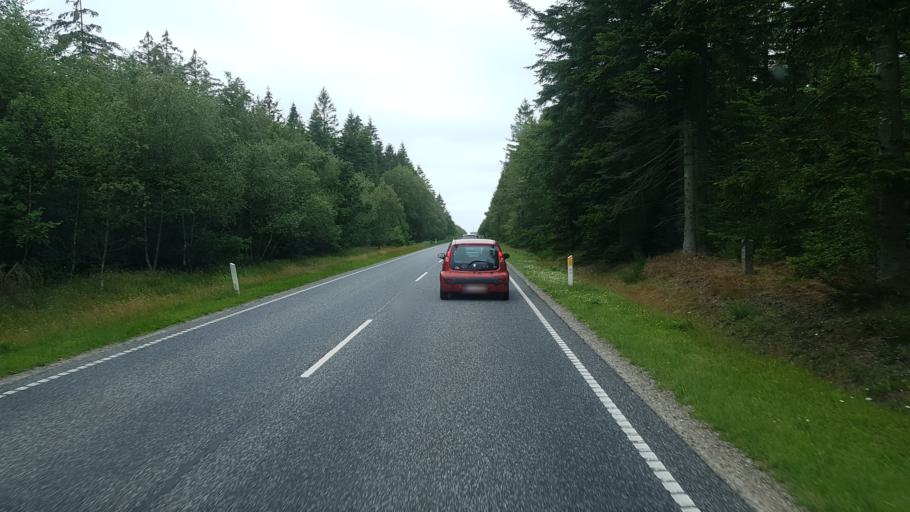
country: DK
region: Central Jutland
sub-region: Lemvig Kommune
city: Lemvig
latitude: 56.4670
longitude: 8.3189
